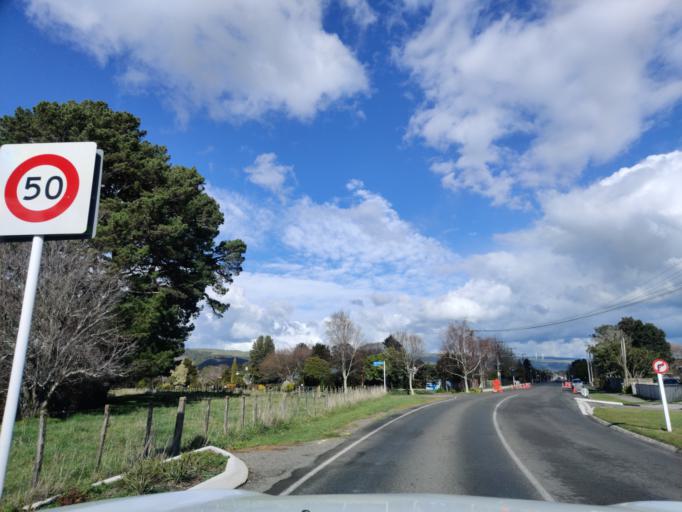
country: NZ
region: Manawatu-Wanganui
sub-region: Palmerston North City
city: Palmerston North
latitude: -40.2815
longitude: 175.7606
